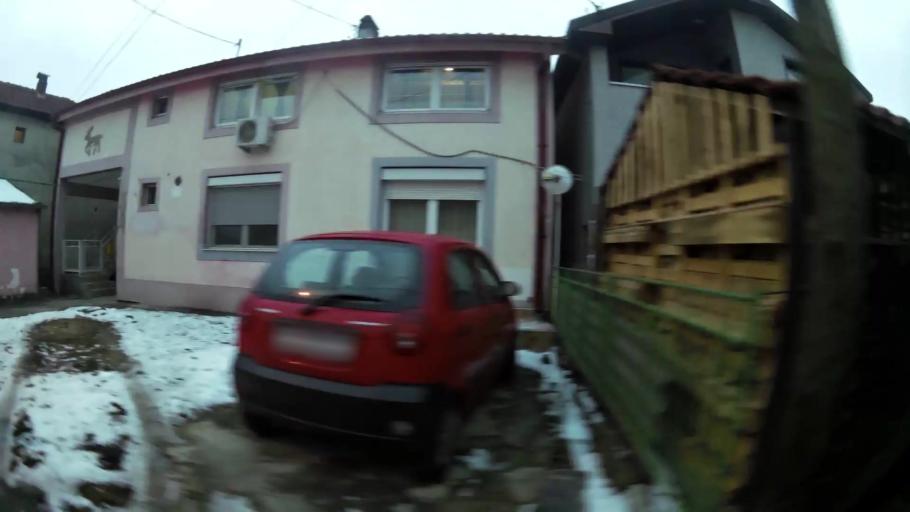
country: MK
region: Kisela Voda
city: Usje
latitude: 41.9751
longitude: 21.4828
